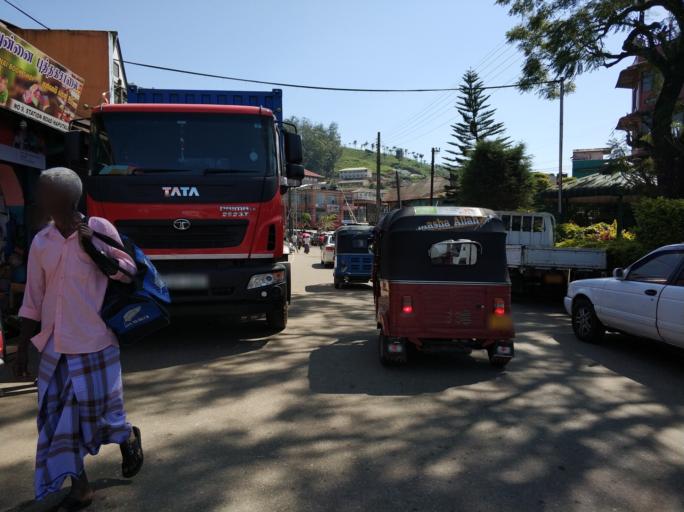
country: LK
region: Uva
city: Haputale
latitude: 6.7689
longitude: 80.9591
